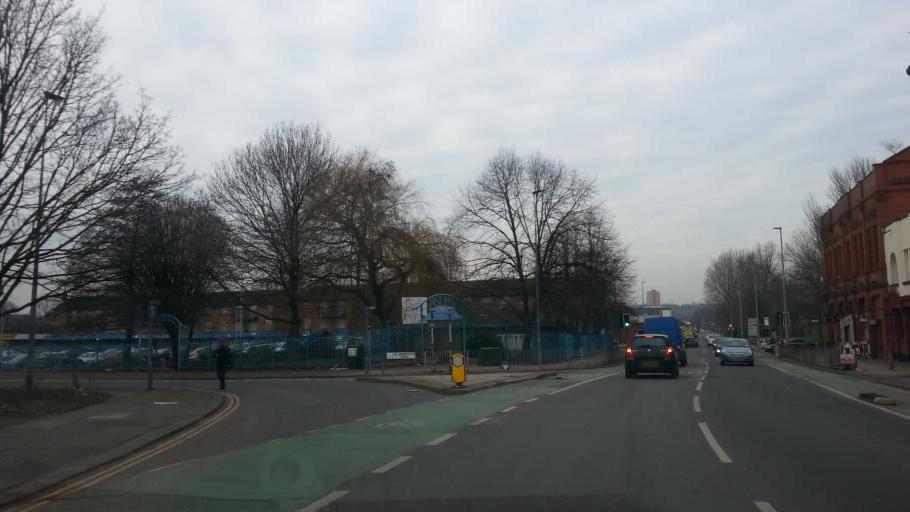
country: GB
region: England
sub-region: Manchester
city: Cheetham Hill
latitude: 53.4907
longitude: -2.2595
